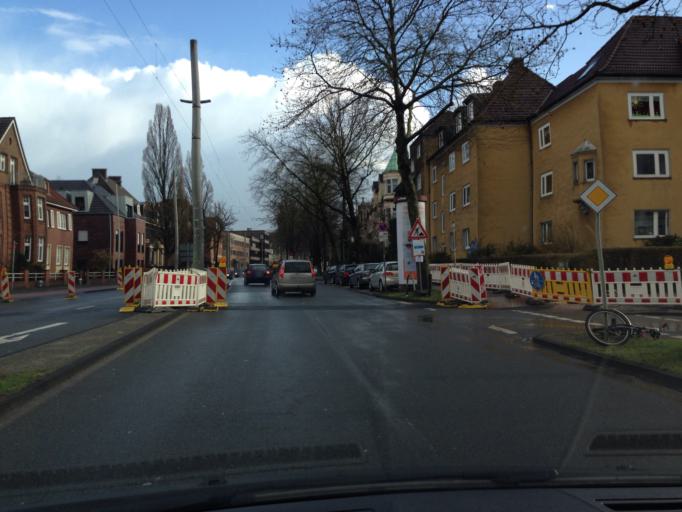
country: DE
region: North Rhine-Westphalia
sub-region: Regierungsbezirk Munster
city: Muenster
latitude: 51.9671
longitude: 7.6457
